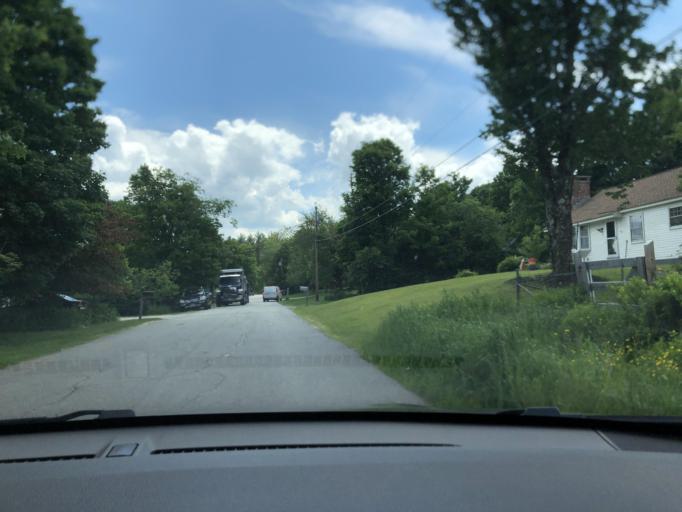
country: US
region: New Hampshire
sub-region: Merrimack County
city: New London
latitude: 43.4062
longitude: -71.9895
